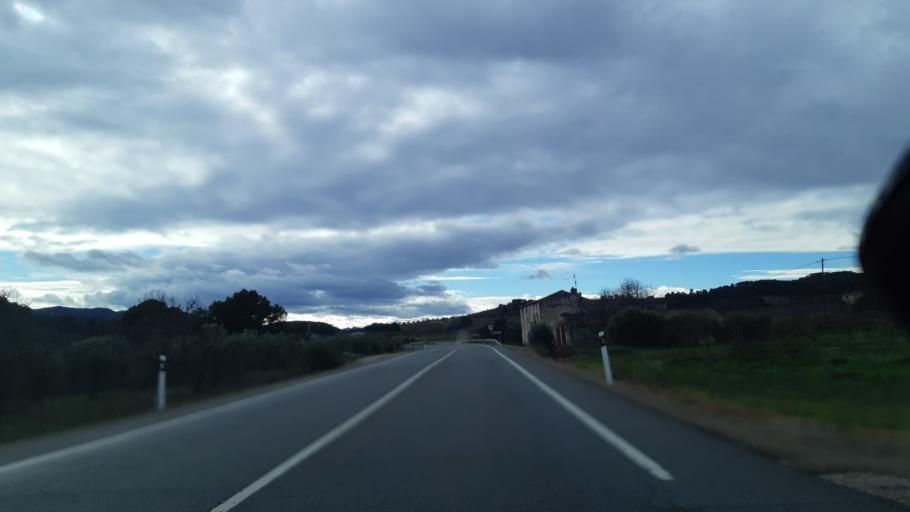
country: ES
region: Catalonia
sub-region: Provincia de Tarragona
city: la Fatarella
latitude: 41.1095
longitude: 0.5310
